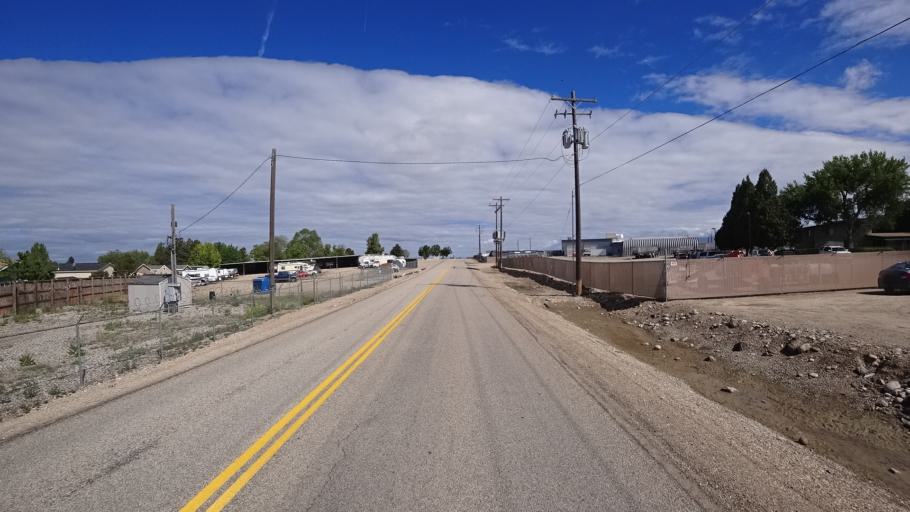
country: US
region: Idaho
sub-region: Ada County
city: Boise
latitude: 43.5260
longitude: -116.1544
